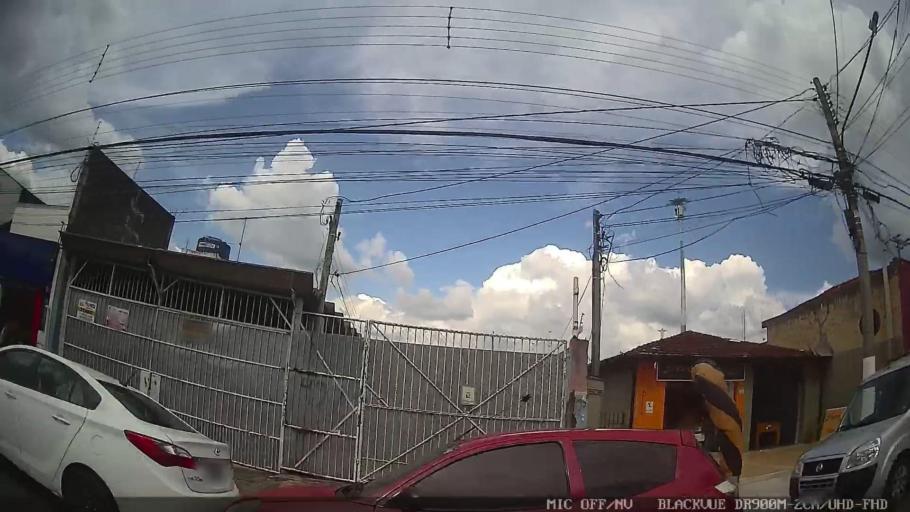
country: BR
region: Sao Paulo
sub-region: Atibaia
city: Atibaia
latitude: -23.1207
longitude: -46.5673
